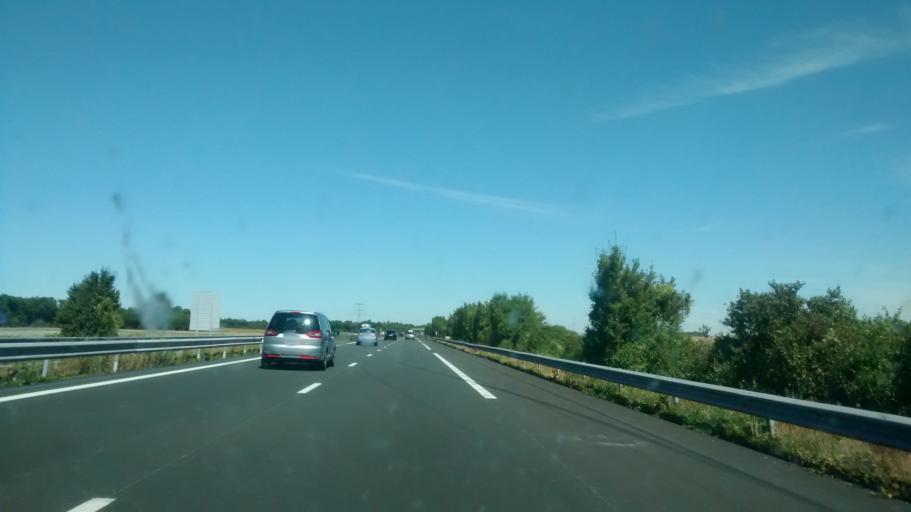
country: FR
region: Poitou-Charentes
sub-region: Departement des Deux-Sevres
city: Beauvoir-sur-Niort
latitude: 46.1594
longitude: -0.5153
